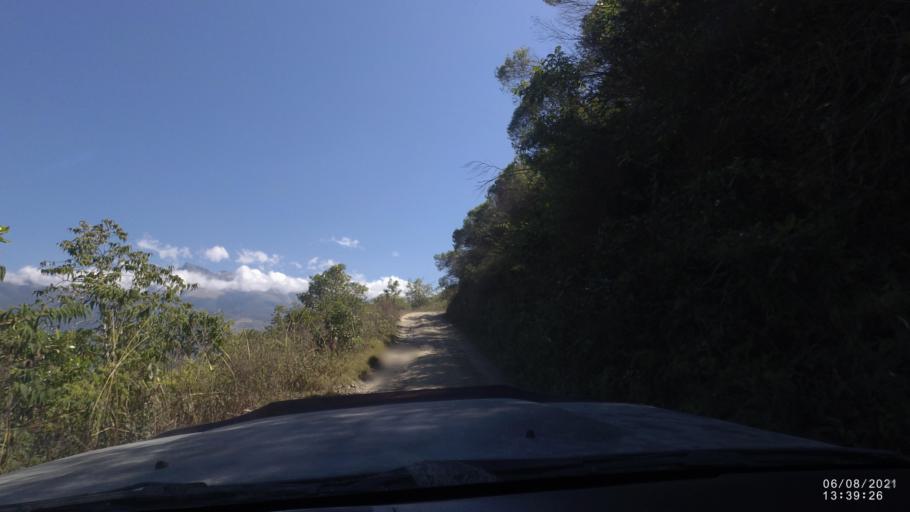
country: BO
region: La Paz
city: Quime
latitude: -16.6858
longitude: -66.7284
